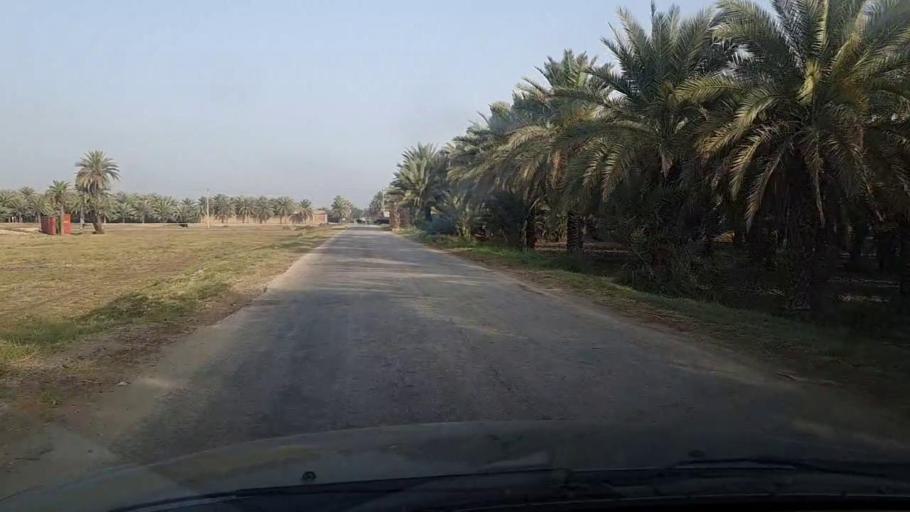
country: PK
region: Sindh
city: Khairpur
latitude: 27.5425
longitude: 68.7057
